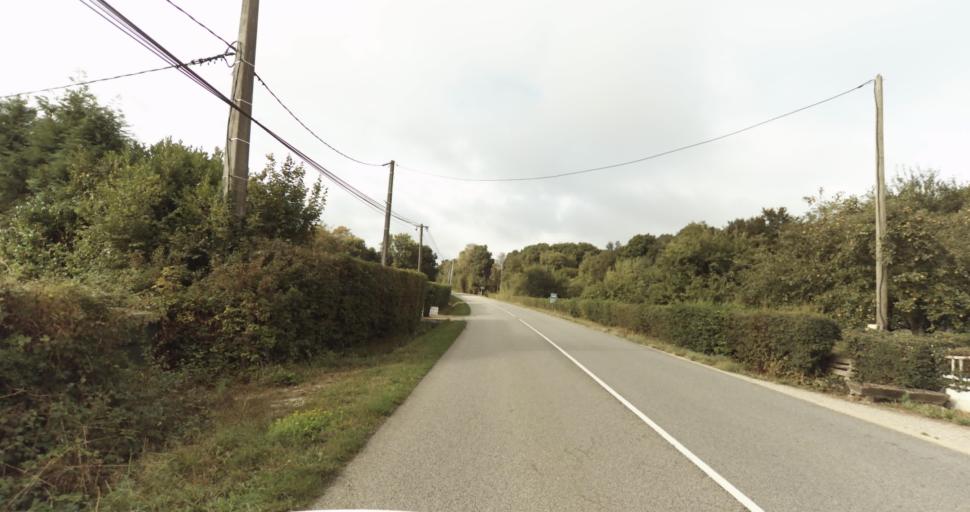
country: FR
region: Lower Normandy
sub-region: Departement de l'Orne
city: Vimoutiers
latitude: 48.9223
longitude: 0.1545
